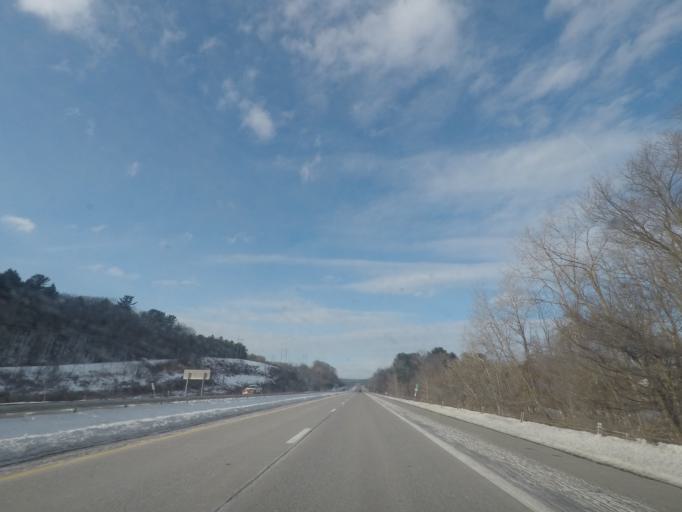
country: US
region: New York
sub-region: Schenectady County
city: Scotia
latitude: 42.8224
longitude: -73.9899
